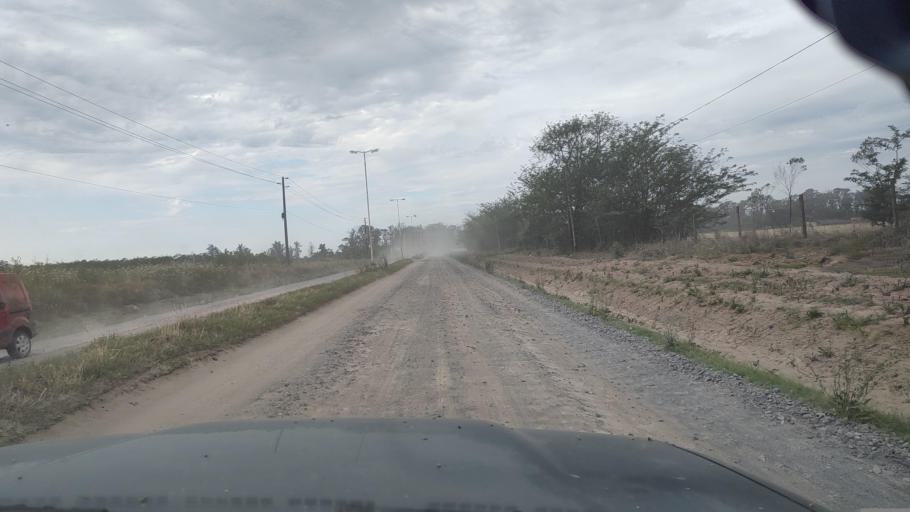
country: AR
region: Buenos Aires
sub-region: Partido de Lujan
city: Lujan
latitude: -34.5485
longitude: -59.0838
